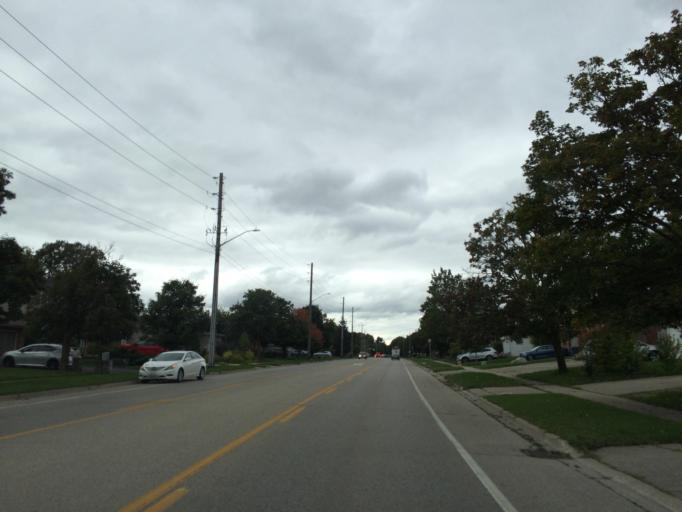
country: CA
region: Ontario
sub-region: Wellington County
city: Guelph
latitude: 43.5213
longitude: -80.2714
